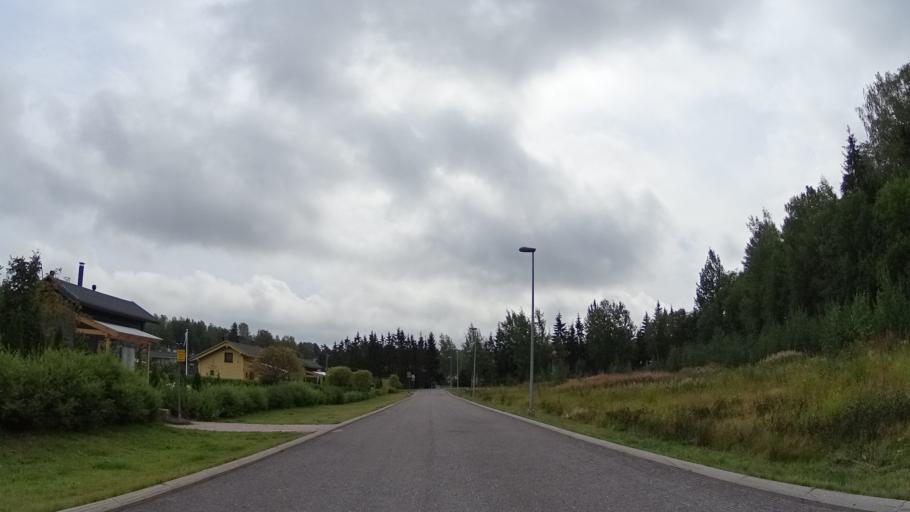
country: FI
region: Uusimaa
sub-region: Helsinki
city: Kilo
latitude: 60.2127
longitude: 24.7948
